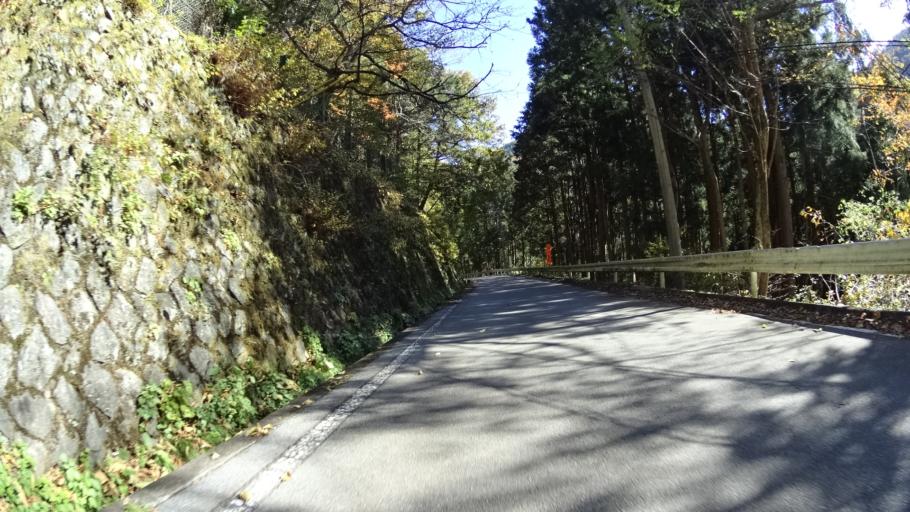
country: JP
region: Yamanashi
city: Otsuki
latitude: 35.7837
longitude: 138.9220
